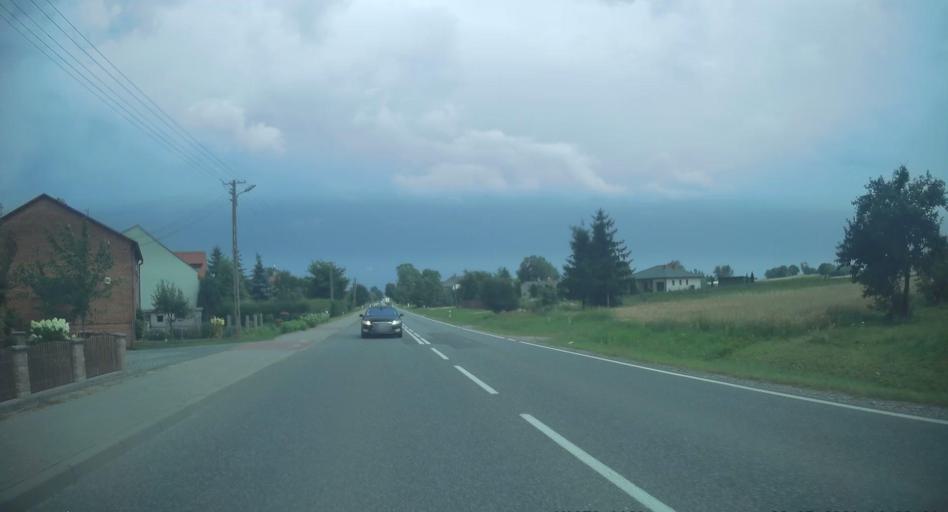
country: PL
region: Lodz Voivodeship
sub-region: Powiat skierniewicki
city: Gluchow
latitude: 51.7740
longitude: 20.1318
